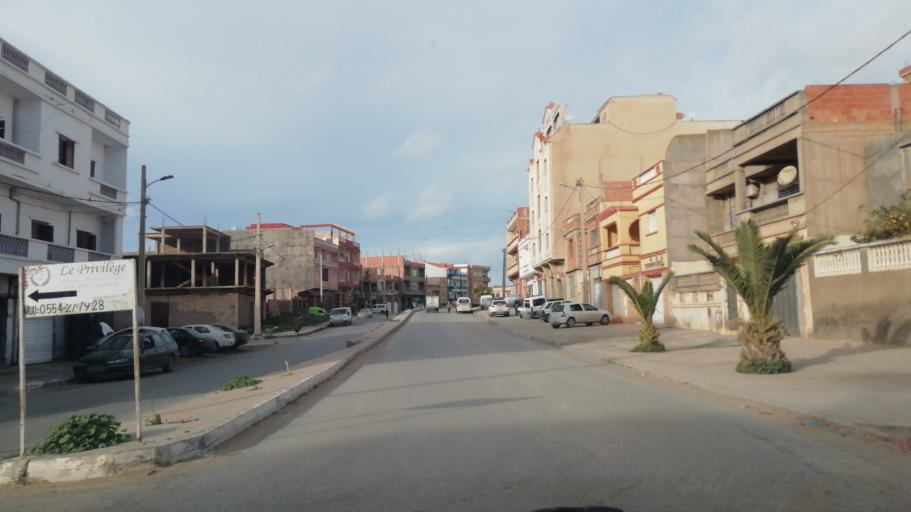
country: DZ
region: Oran
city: Bir el Djir
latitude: 35.7340
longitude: -0.5726
